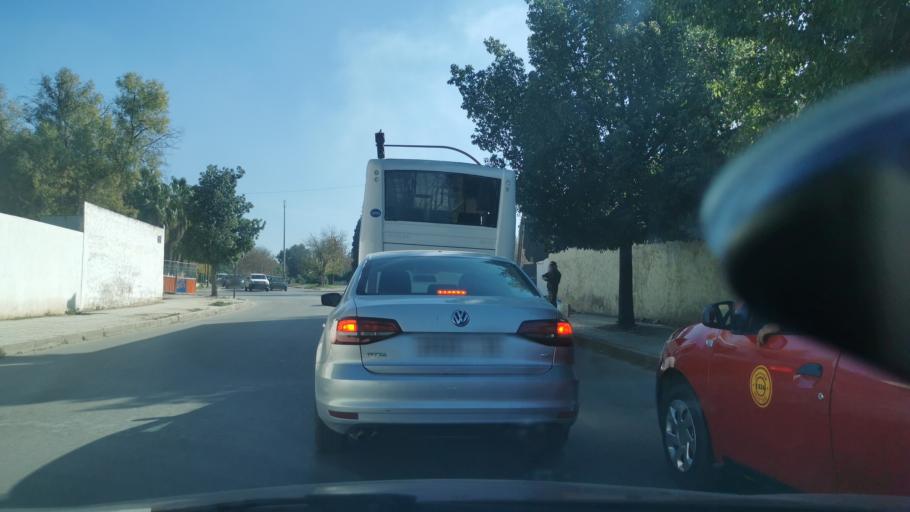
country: MA
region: Fes-Boulemane
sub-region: Fes
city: Fes
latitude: 34.0324
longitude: -4.9882
